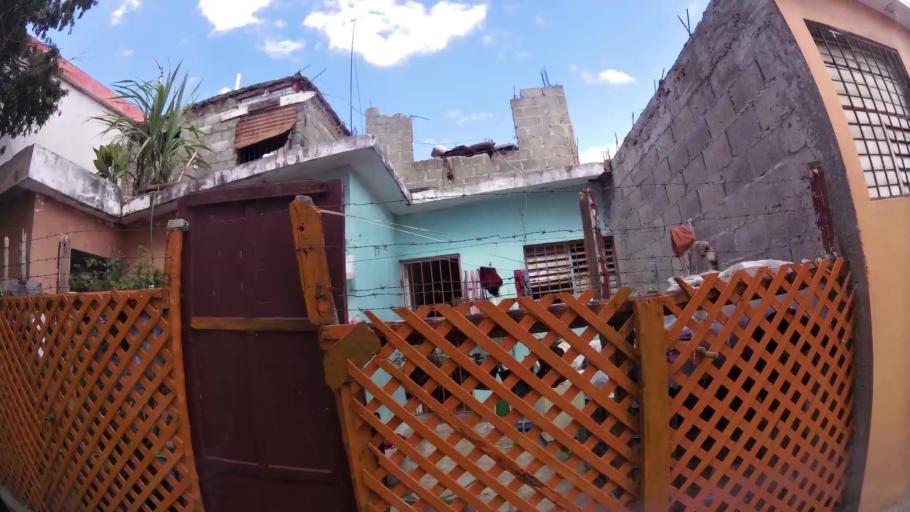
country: DO
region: San Cristobal
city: San Cristobal
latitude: 18.4267
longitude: -70.1156
